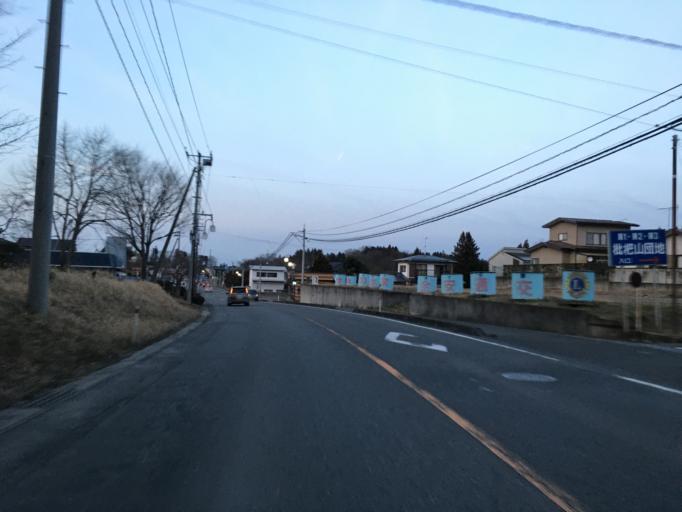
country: JP
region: Fukushima
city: Ishikawa
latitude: 37.1123
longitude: 140.3496
